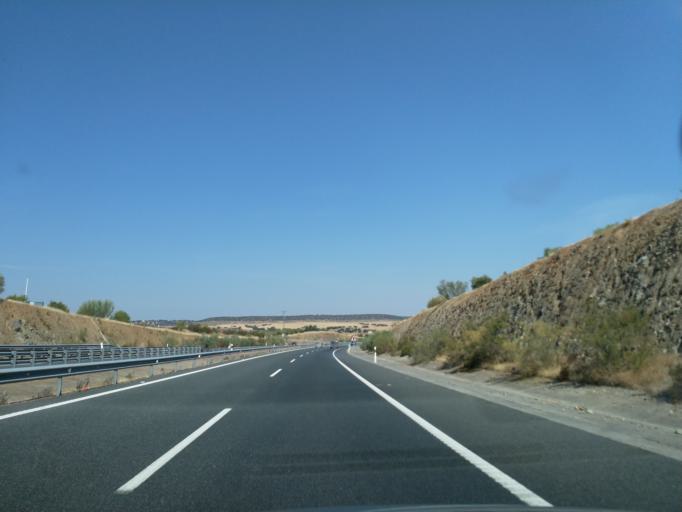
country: ES
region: Extremadura
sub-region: Provincia de Badajoz
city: Aljucen
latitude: 39.0393
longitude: -6.3382
